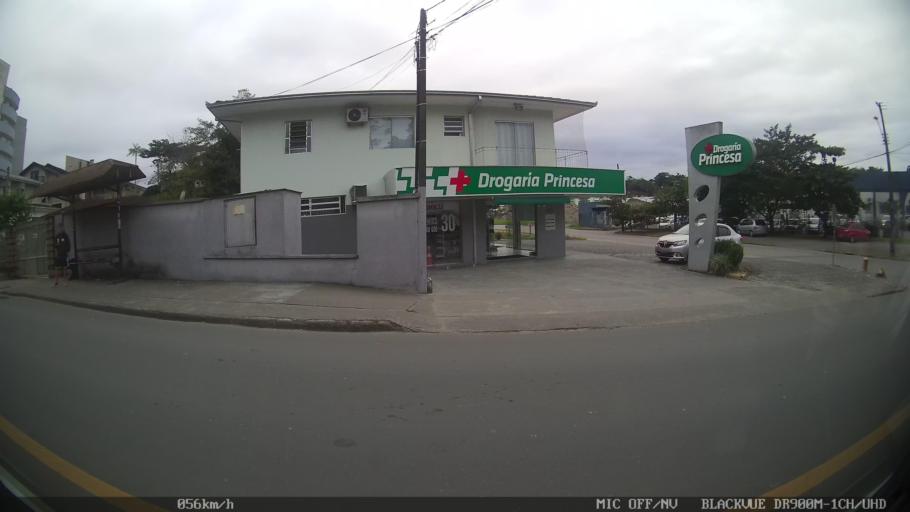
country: BR
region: Santa Catarina
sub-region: Joinville
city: Joinville
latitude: -26.2784
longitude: -48.8655
